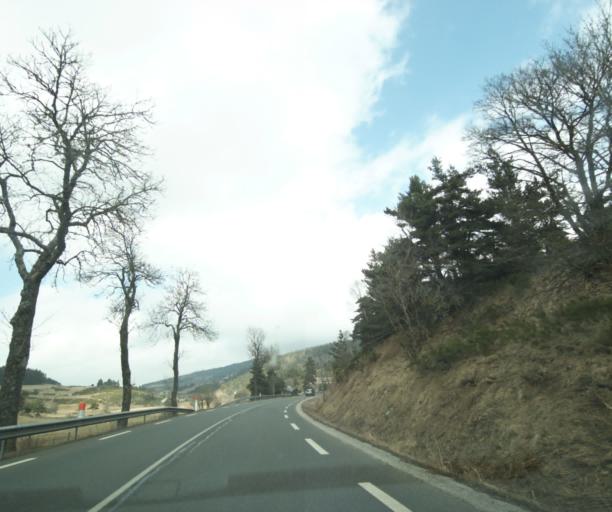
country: FR
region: Languedoc-Roussillon
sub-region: Departement de la Lozere
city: Mende
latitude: 44.6014
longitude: 3.6727
